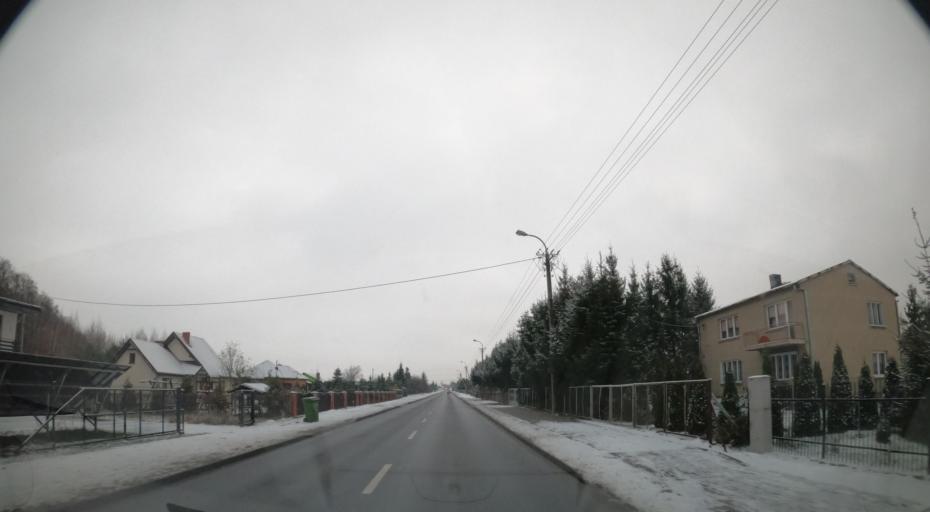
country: PL
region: Kujawsko-Pomorskie
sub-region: Powiat lipnowski
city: Wielgie
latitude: 52.7448
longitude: 19.2556
